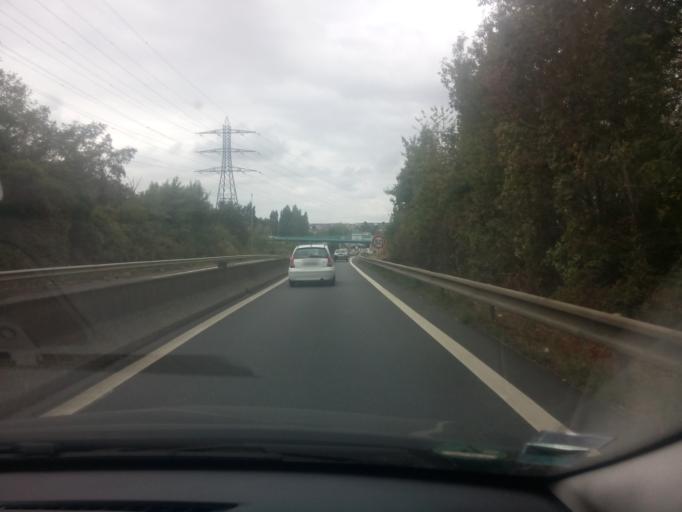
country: FR
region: Ile-de-France
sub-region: Departement de l'Essonne
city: Palaiseau
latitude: 48.7218
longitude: 2.2507
